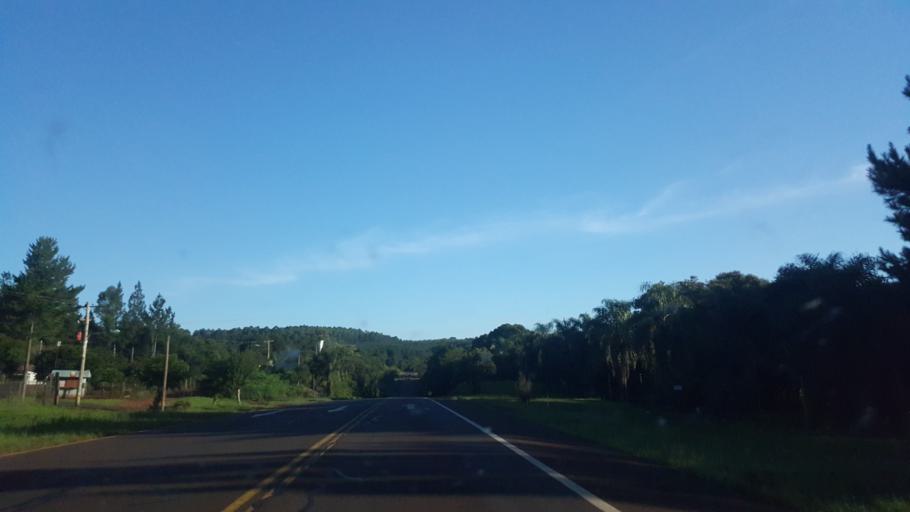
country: AR
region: Misiones
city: Caraguatay
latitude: -26.6546
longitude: -54.7539
